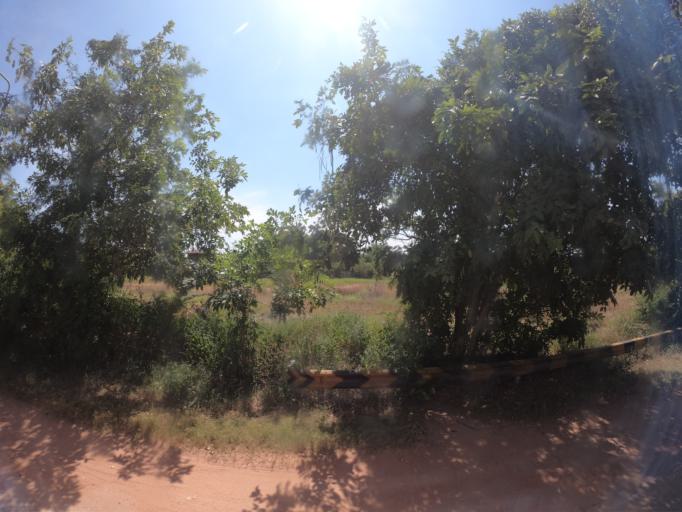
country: TH
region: Khon Kaen
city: Ban Phai
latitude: 16.0628
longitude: 102.7244
